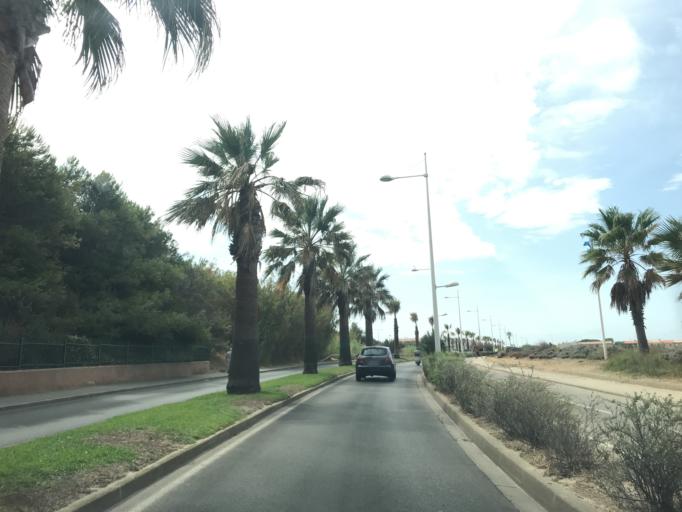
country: FR
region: Provence-Alpes-Cote d'Azur
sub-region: Departement du Var
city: Sanary-sur-Mer
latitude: 43.0953
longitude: 5.8129
